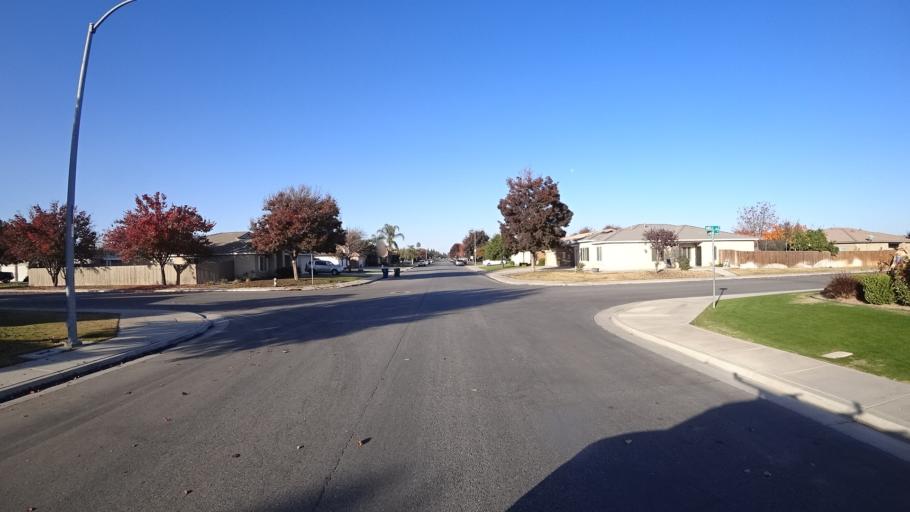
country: US
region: California
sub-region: Kern County
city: Greenfield
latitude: 35.2778
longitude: -119.0277
